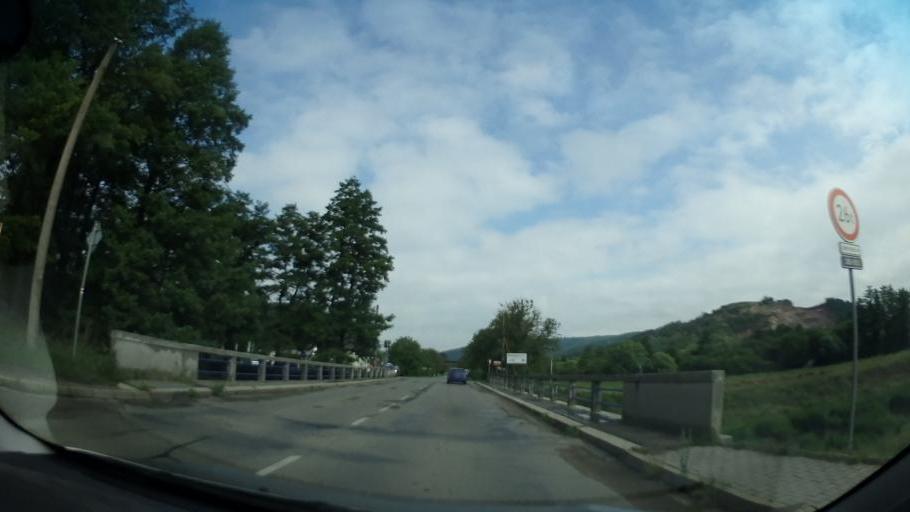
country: CZ
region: South Moravian
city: Predklasteri
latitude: 49.3559
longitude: 16.4015
